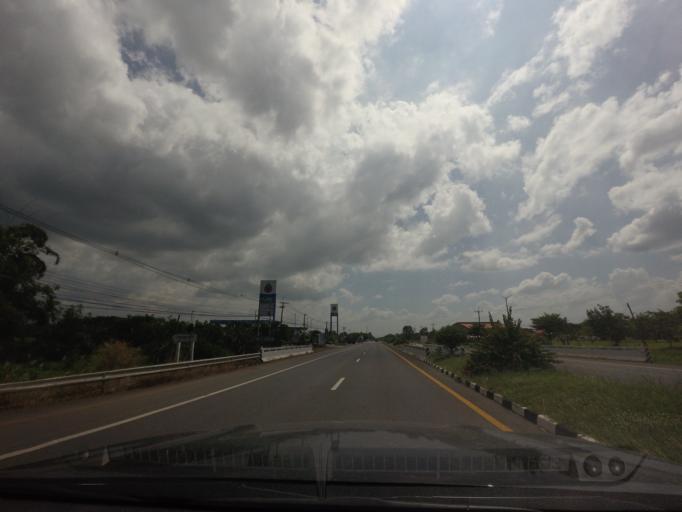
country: TH
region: Phetchabun
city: Nong Phai
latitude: 16.2055
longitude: 101.0890
